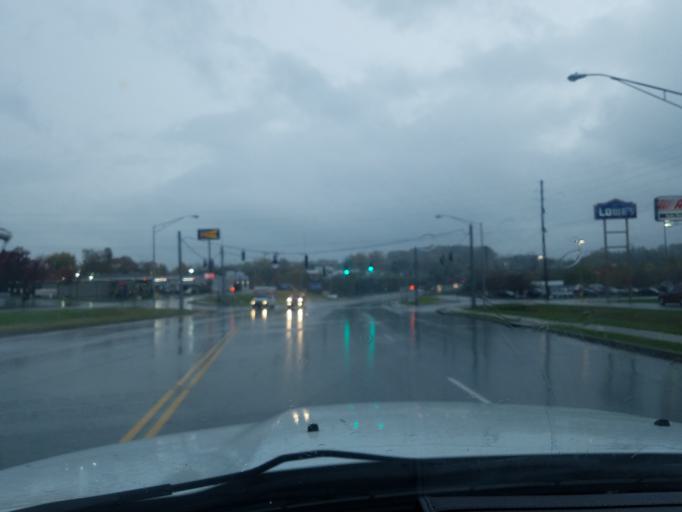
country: US
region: Kentucky
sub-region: Taylor County
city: Campbellsville
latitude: 37.3416
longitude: -85.3627
